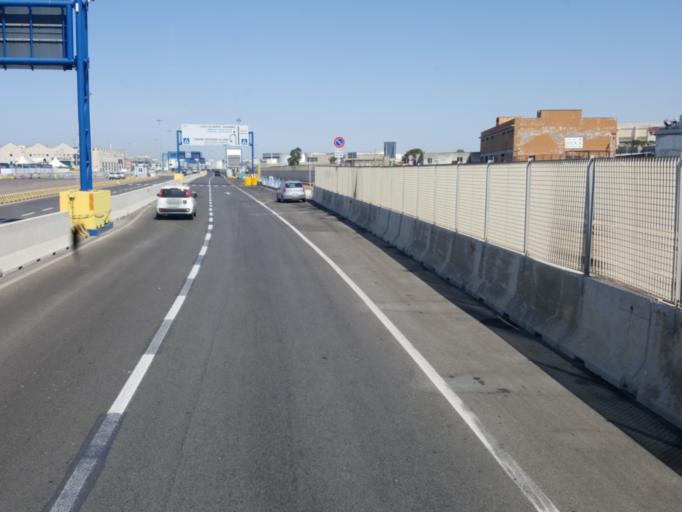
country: IT
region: Latium
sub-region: Citta metropolitana di Roma Capitale
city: Civitavecchia
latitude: 42.0985
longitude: 11.7849
